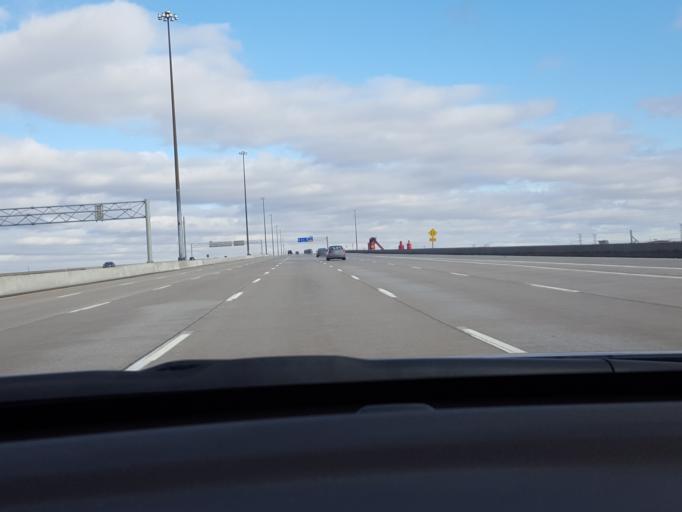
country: CA
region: Ontario
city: Concord
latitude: 43.7877
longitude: -79.5162
